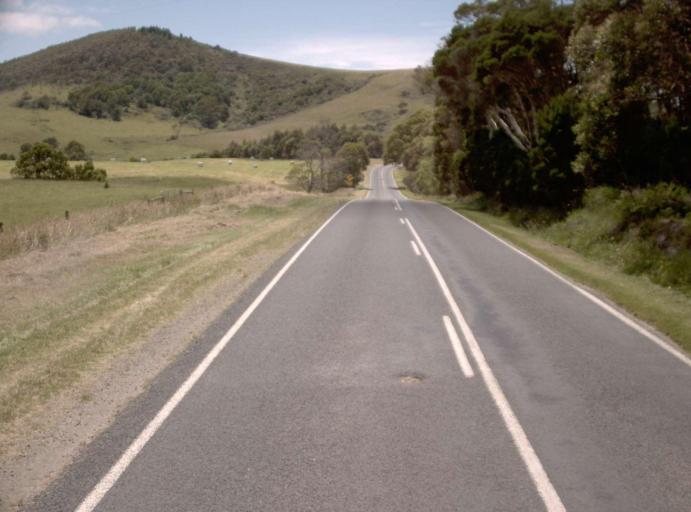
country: AU
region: Victoria
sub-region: Bass Coast
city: North Wonthaggi
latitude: -38.7173
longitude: 146.1091
